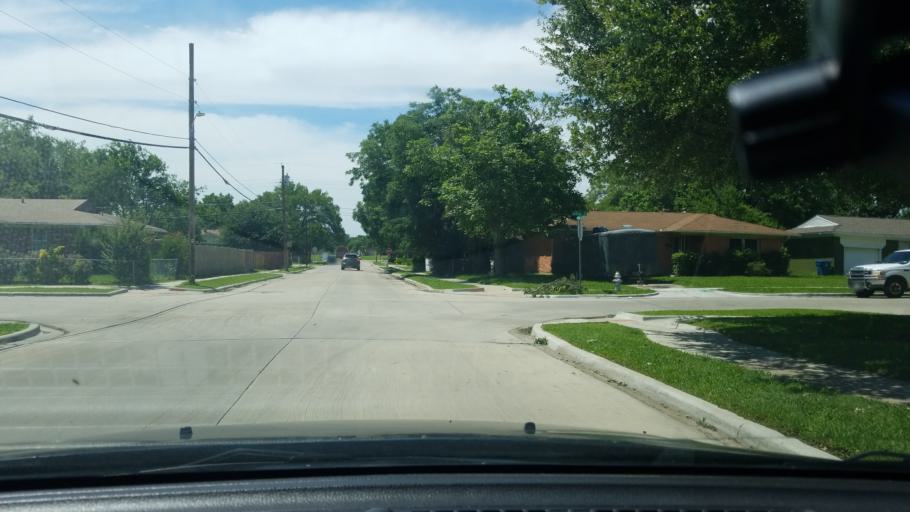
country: US
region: Texas
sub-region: Dallas County
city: Mesquite
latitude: 32.7877
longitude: -96.6128
